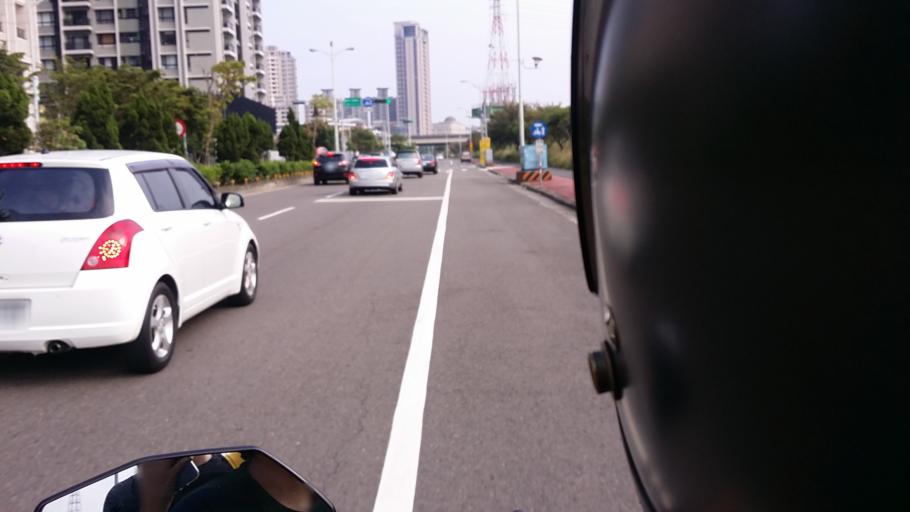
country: TW
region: Taiwan
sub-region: Hsinchu
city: Zhubei
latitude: 24.8184
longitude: 121.0103
